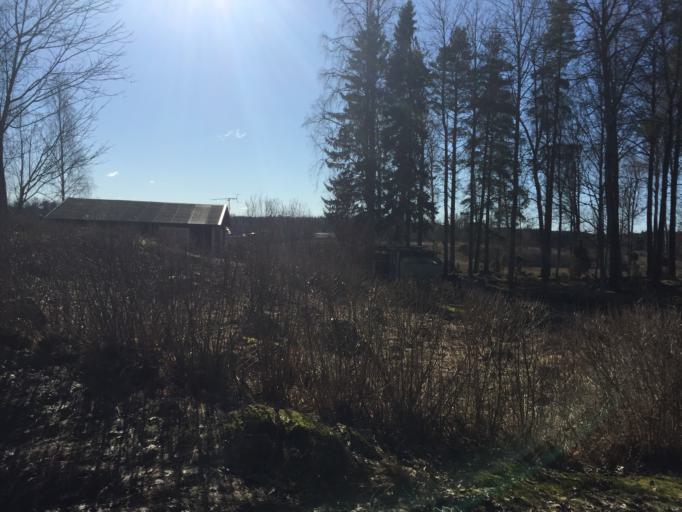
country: SE
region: OEstergoetland
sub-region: Finspangs Kommun
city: Finspang
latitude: 58.8986
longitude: 15.6893
